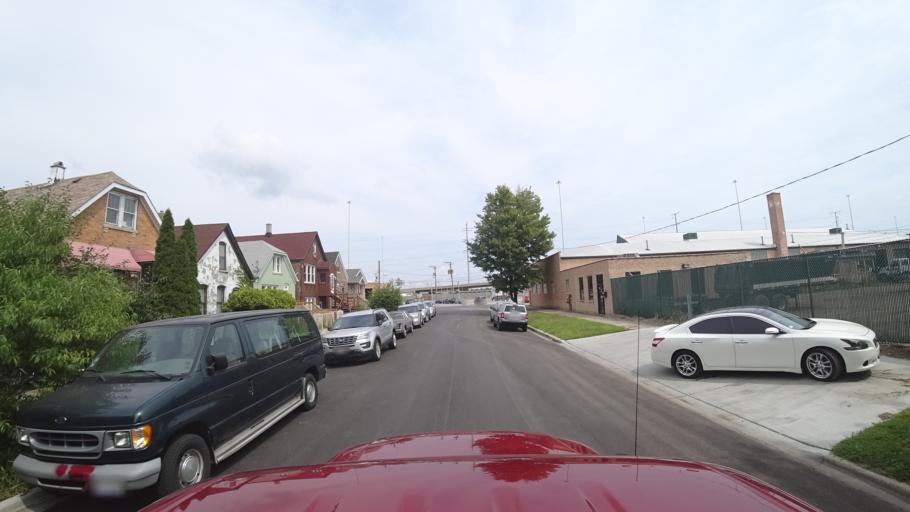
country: US
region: Illinois
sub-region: Cook County
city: Chicago
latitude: 41.8352
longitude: -87.6779
